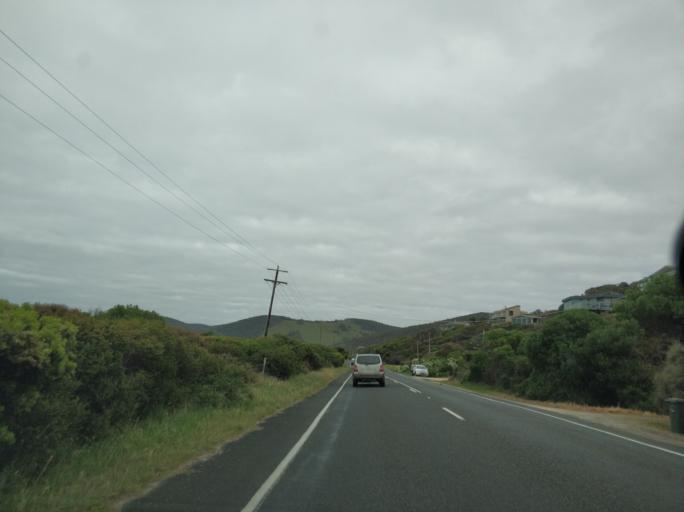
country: AU
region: Victoria
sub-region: Surf Coast
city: Anglesea
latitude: -38.4701
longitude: 144.0551
